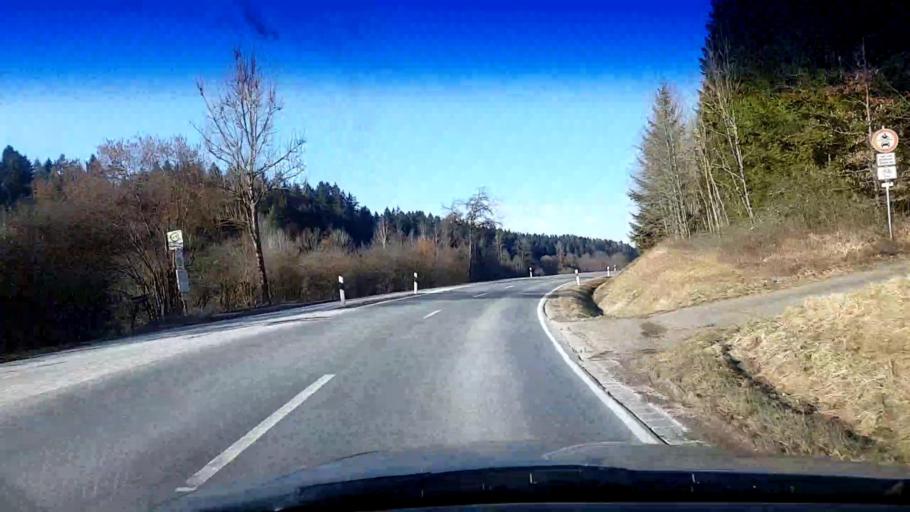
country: DE
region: Bavaria
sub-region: Upper Franconia
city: Aufsess
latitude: 49.8941
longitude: 11.2241
